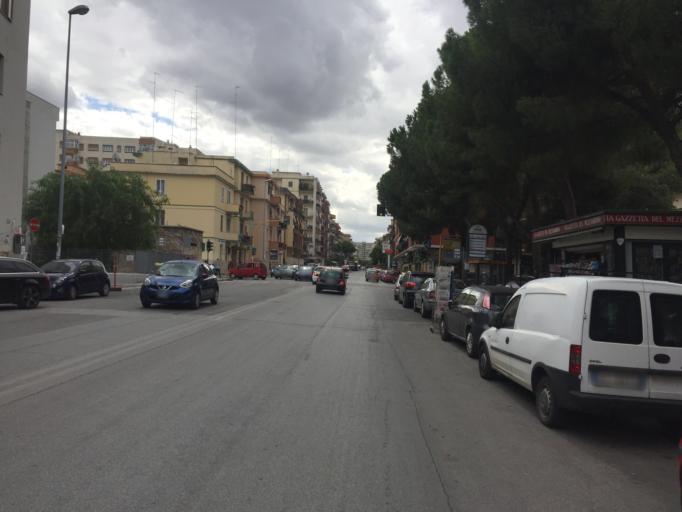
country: IT
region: Apulia
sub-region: Provincia di Bari
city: Bari
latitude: 41.1060
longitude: 16.8598
